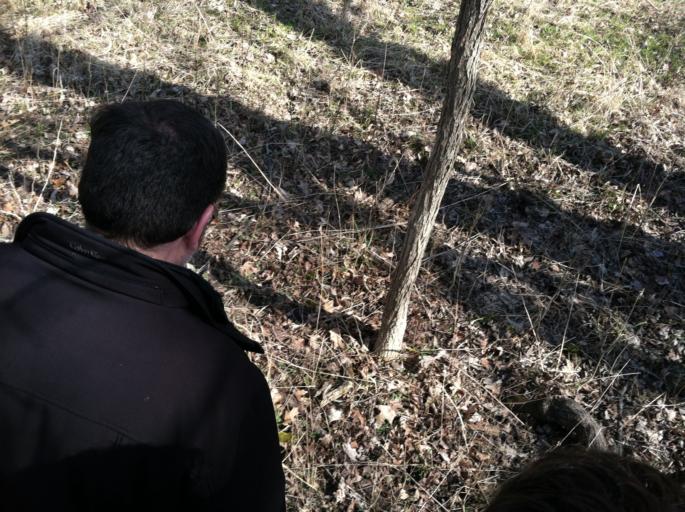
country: US
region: Illinois
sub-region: Cook County
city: River Forest
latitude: 41.9003
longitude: -87.8307
